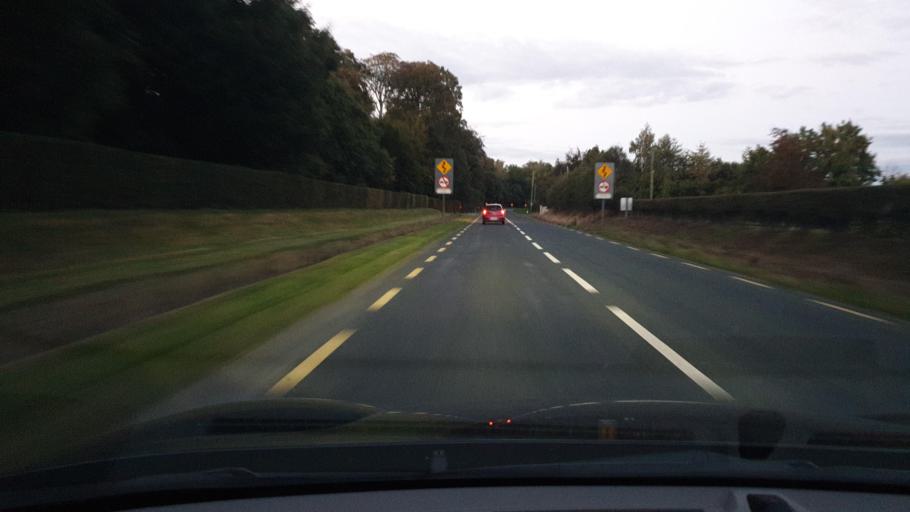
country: IE
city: Confey
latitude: 53.4069
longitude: -6.5203
